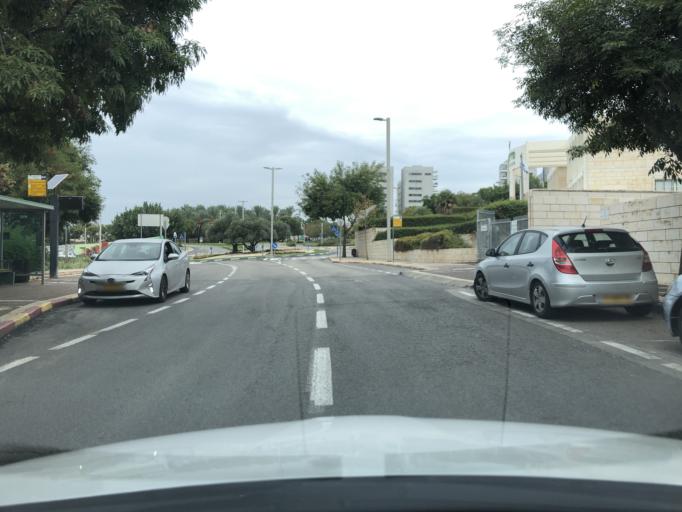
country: IL
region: Central District
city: Modiin
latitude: 31.9071
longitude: 35.0075
